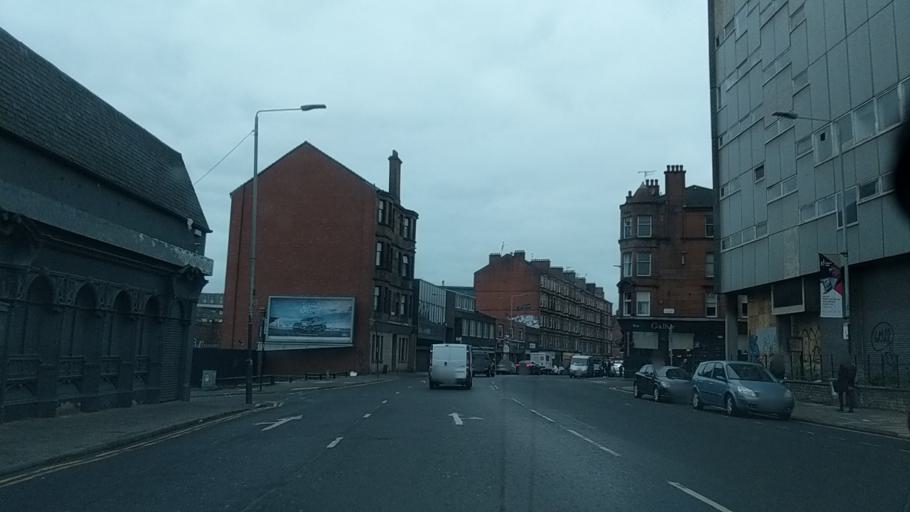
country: GB
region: Scotland
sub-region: Glasgow City
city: Glasgow
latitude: 55.8700
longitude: -4.2965
